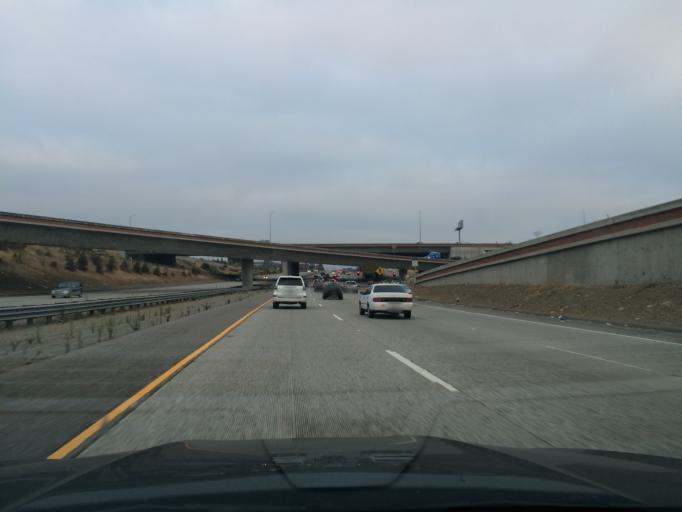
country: US
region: California
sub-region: Santa Clara County
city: Cambrian Park
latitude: 37.2550
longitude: -121.9532
